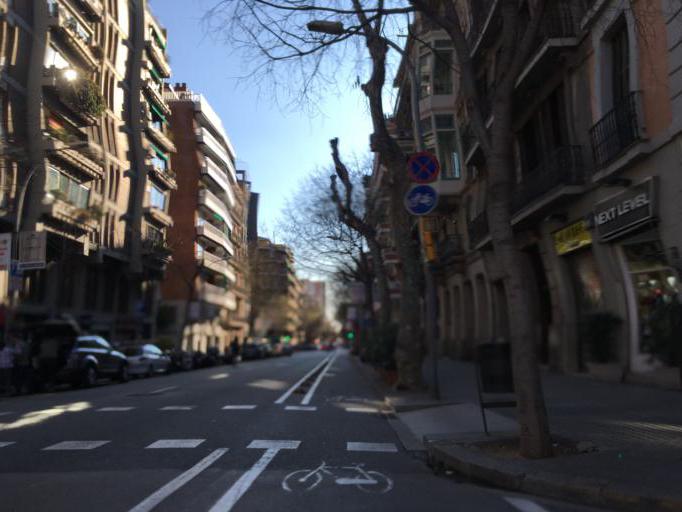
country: ES
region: Catalonia
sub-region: Provincia de Barcelona
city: Eixample
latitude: 41.3856
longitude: 2.1607
